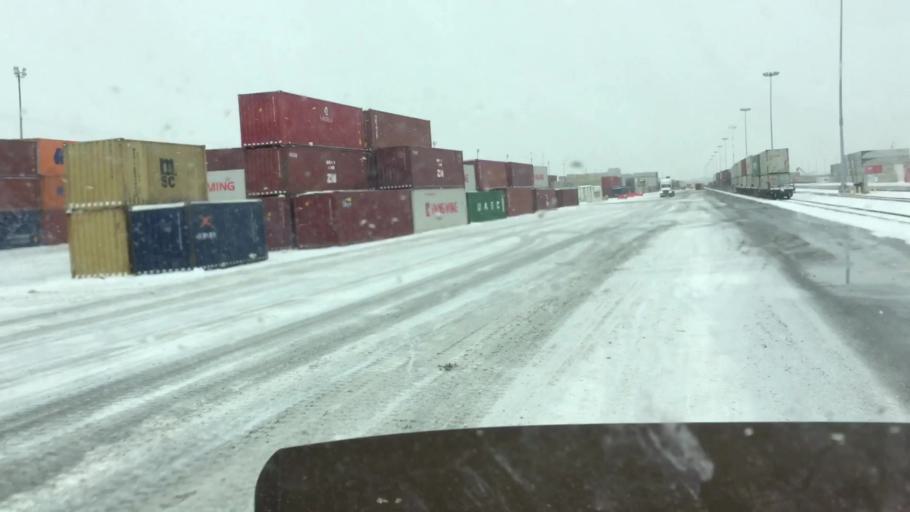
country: CA
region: Quebec
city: Cote-Saint-Luc
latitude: 45.4628
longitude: -73.6918
